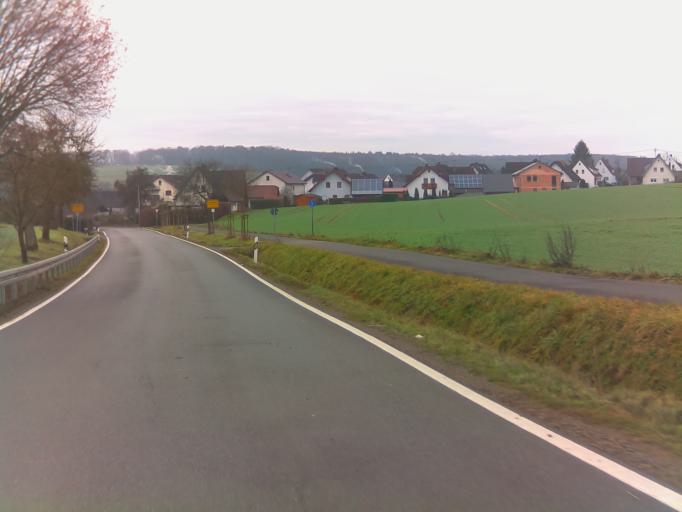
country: DE
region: Bavaria
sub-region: Regierungsbezirk Unterfranken
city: Schonau
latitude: 50.0777
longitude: 9.7503
